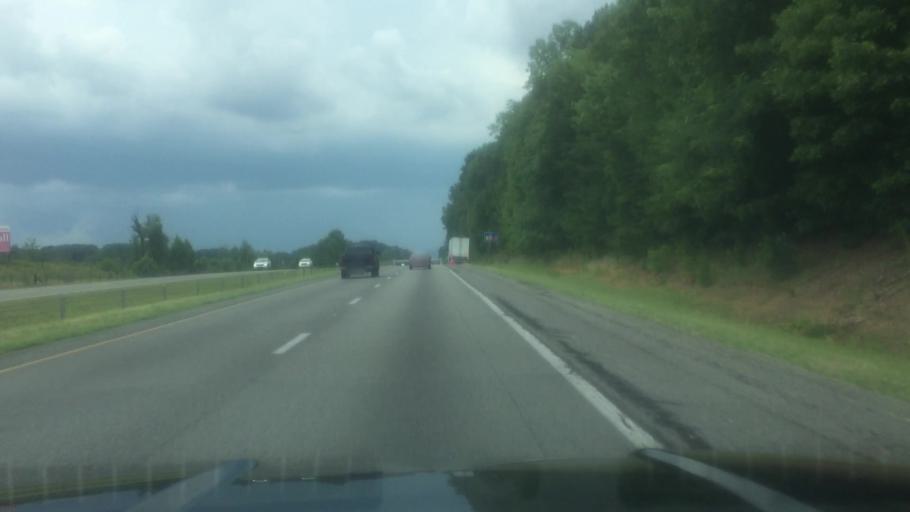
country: US
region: North Carolina
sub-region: Surry County
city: Pilot Mountain
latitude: 36.3688
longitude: -80.4831
